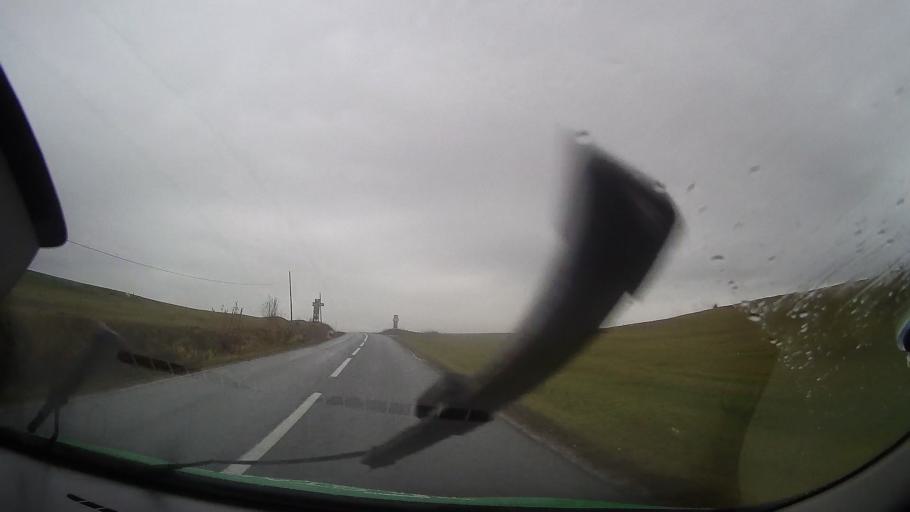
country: RO
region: Bistrita-Nasaud
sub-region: Comuna Monor
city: Monor
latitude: 46.9594
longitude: 24.6721
